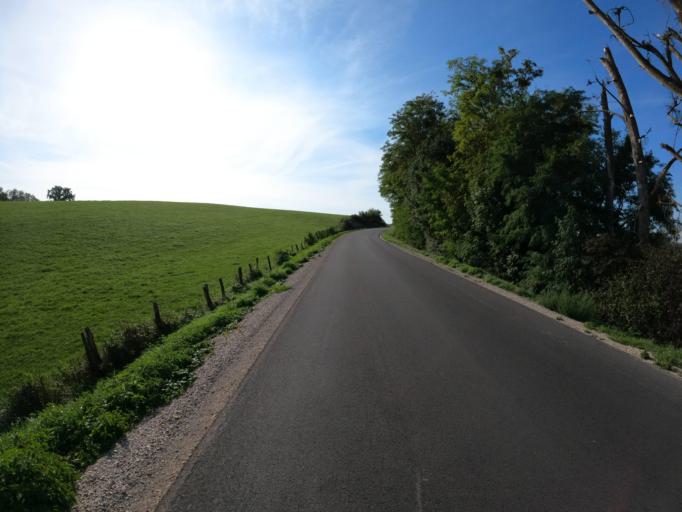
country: FR
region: Franche-Comte
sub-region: Departement du Jura
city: Bletterans
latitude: 46.7348
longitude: 5.5028
